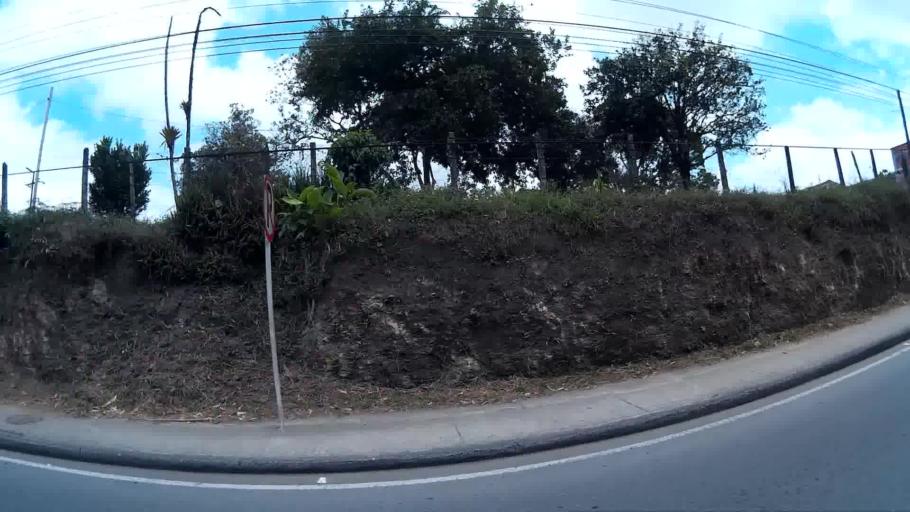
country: CO
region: Quindio
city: Circasia
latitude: 4.5765
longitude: -75.6449
